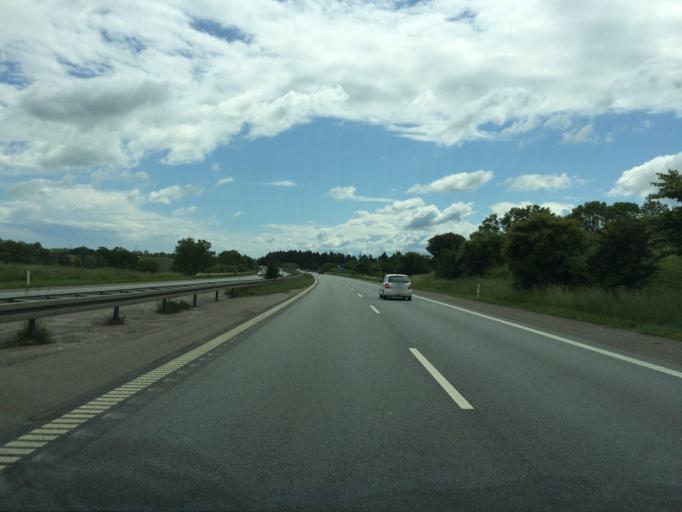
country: DK
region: Zealand
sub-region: Lejre Kommune
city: Lejre
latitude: 55.6308
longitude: 11.9647
